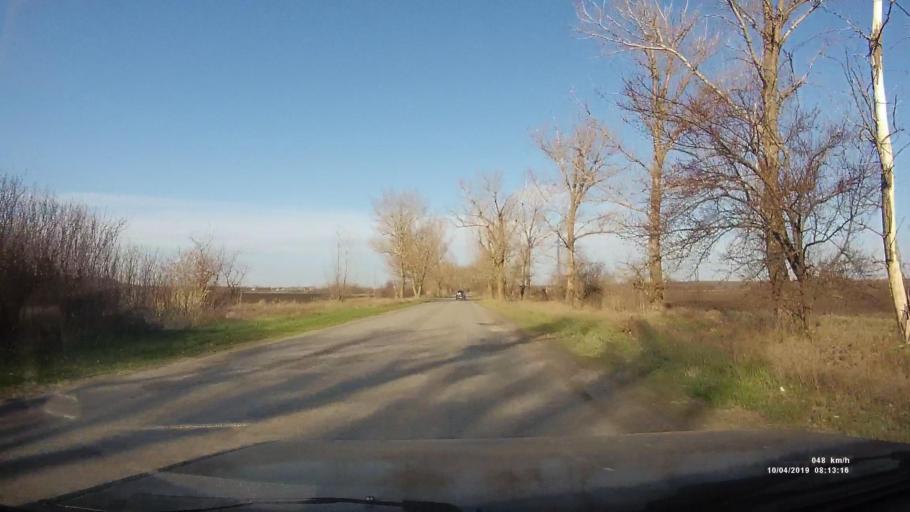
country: RU
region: Rostov
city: Masalovka
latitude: 48.3616
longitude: 40.2484
